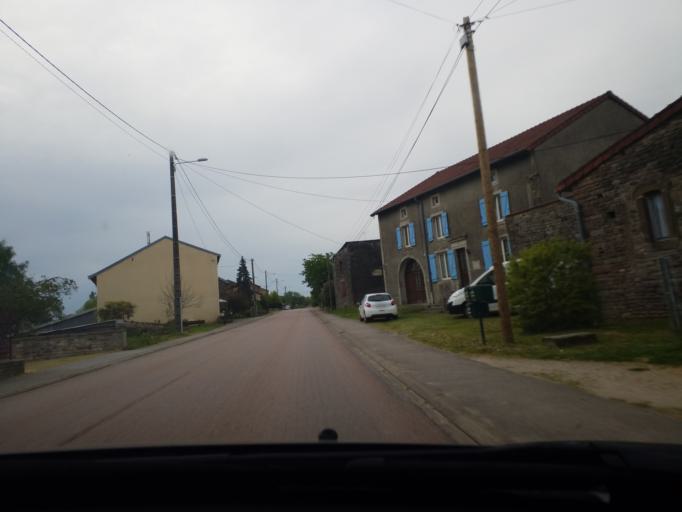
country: FR
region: Lorraine
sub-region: Departement des Vosges
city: Bains-les-Bains
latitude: 48.0355
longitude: 6.1878
